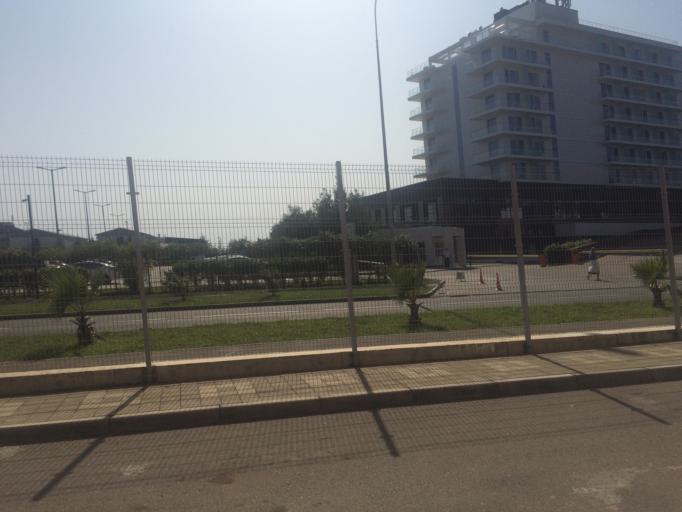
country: RU
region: Krasnodarskiy
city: Adler
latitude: 43.3951
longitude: 39.9781
